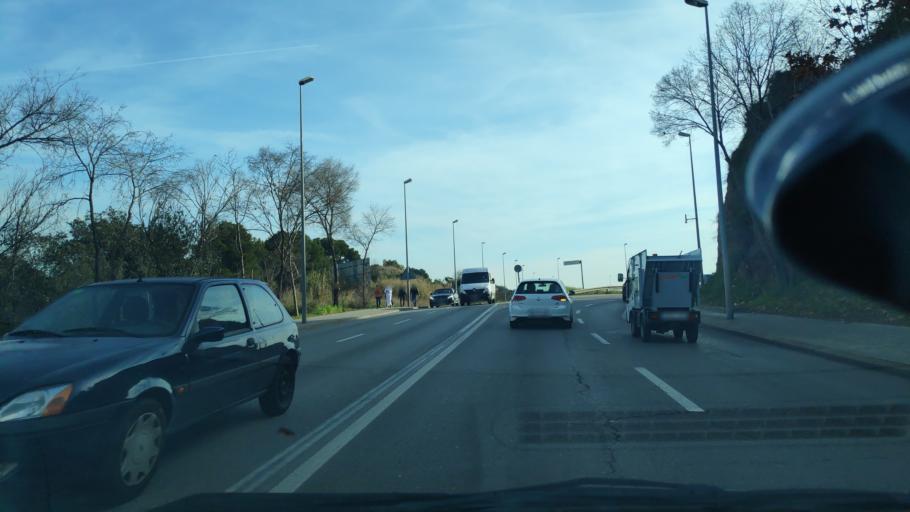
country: ES
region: Catalonia
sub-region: Provincia de Barcelona
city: Sabadell
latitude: 41.5682
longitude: 2.0993
